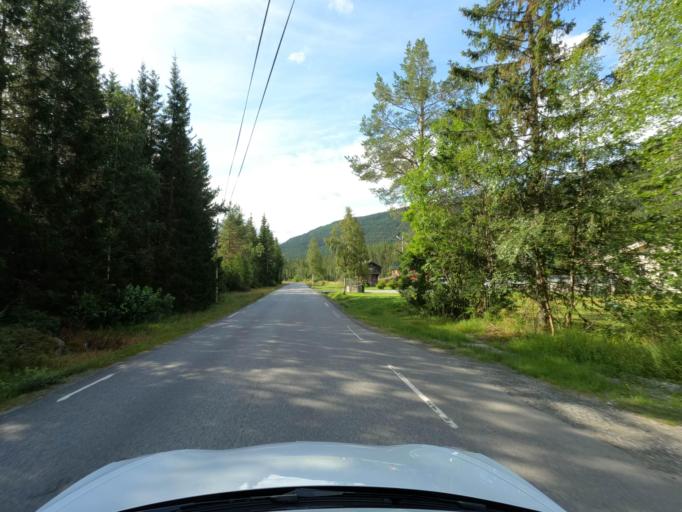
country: NO
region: Buskerud
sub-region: Nore og Uvdal
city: Rodberg
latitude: 60.0920
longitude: 8.7615
